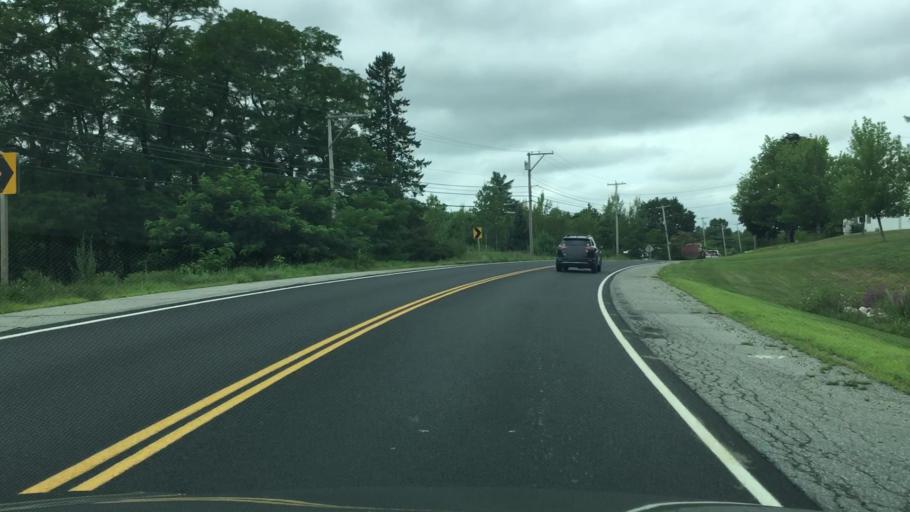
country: US
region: Maine
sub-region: Penobscot County
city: Orrington
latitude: 44.6976
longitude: -68.8194
